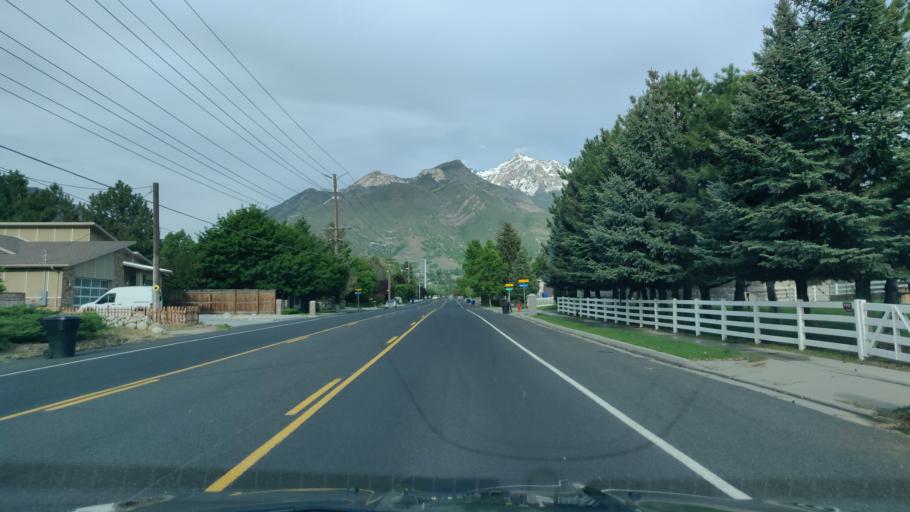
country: US
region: Utah
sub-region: Salt Lake County
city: Little Cottonwood Creek Valley
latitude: 40.6023
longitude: -111.8289
